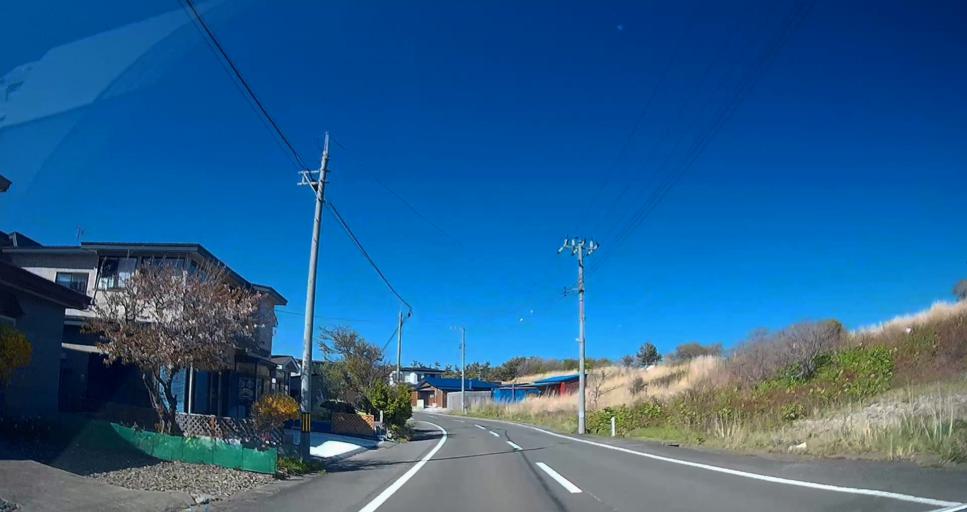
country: JP
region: Hokkaido
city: Hakodate
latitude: 41.5410
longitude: 140.9121
